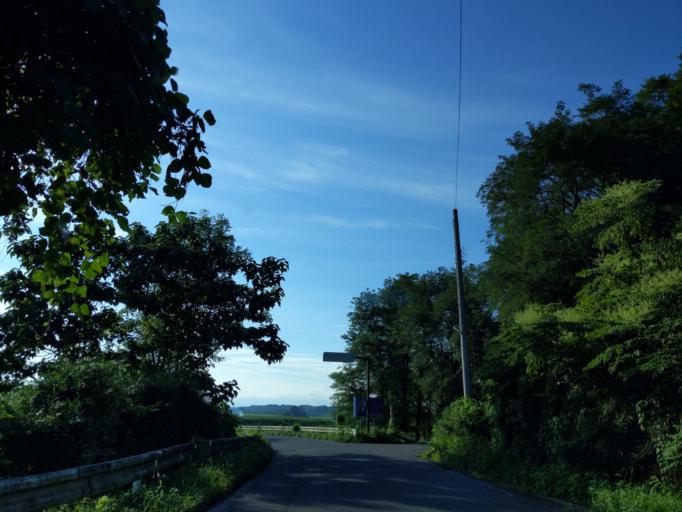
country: JP
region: Fukushima
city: Sukagawa
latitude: 37.2866
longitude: 140.4145
